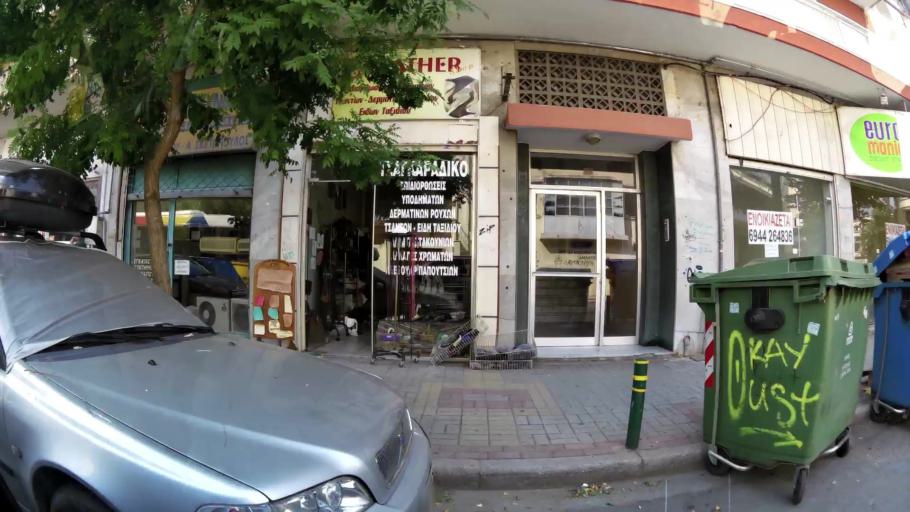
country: GR
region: Central Macedonia
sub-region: Nomos Thessalonikis
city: Sykies
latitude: 40.6468
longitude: 22.9498
